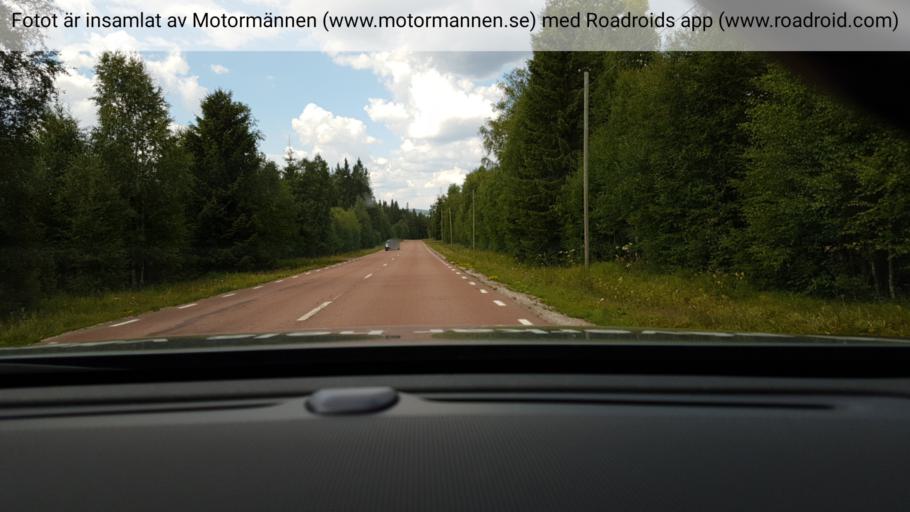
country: SE
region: Dalarna
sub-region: Faluns Kommun
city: Bjursas
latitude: 61.0274
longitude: 15.5203
